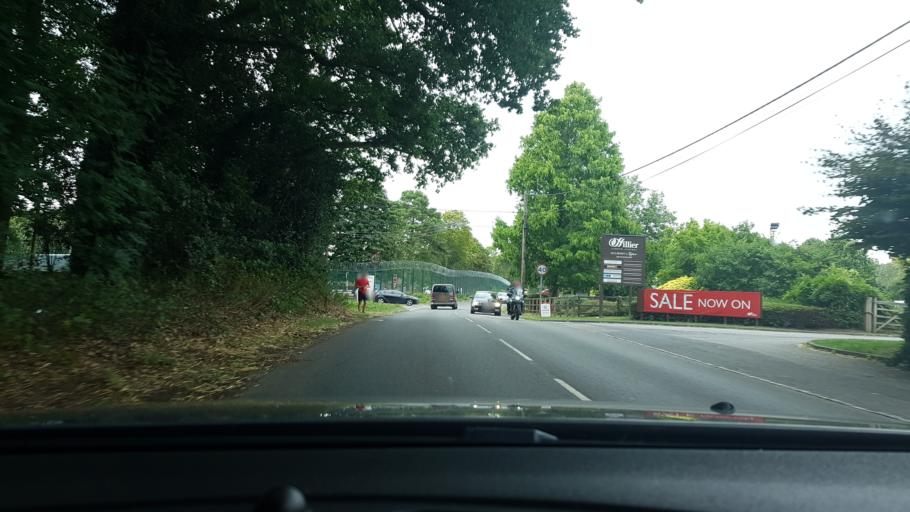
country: GB
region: England
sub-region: West Berkshire
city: Hermitage
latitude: 51.4531
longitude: -1.2807
